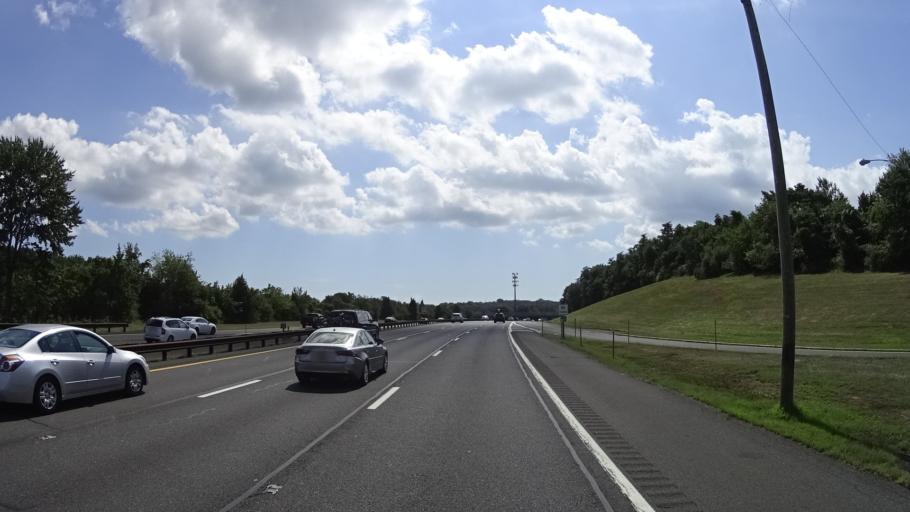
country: US
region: New Jersey
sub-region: Monmouth County
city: Lincroft
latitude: 40.3770
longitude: -74.1510
